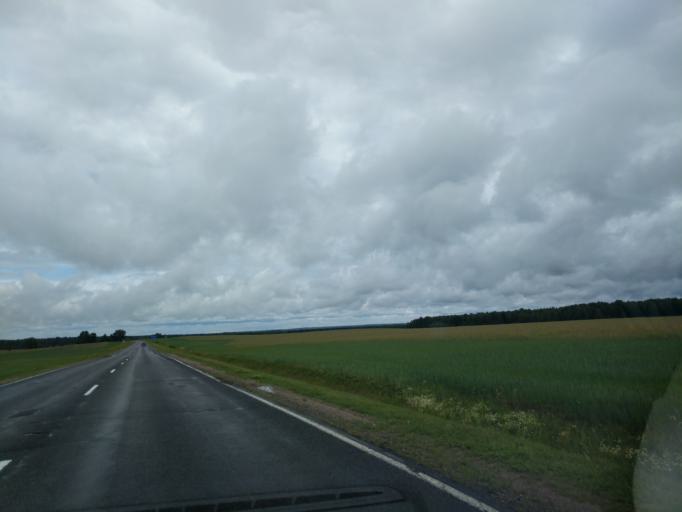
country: BY
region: Minsk
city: Il'ya
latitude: 54.3250
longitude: 27.4659
